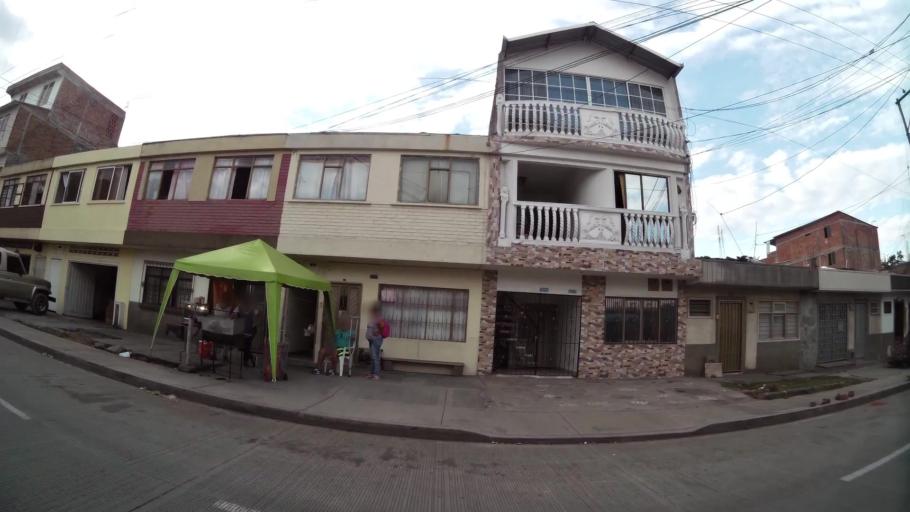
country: CO
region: Valle del Cauca
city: Cali
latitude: 3.4569
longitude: -76.5146
